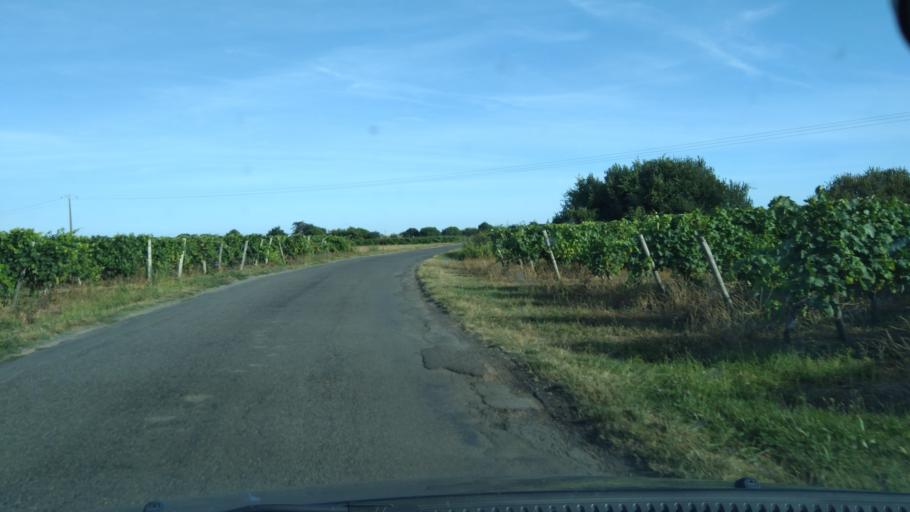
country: FR
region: Poitou-Charentes
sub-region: Departement de la Charente-Maritime
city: Dolus-d'Oleron
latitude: 45.9427
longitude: -1.3409
